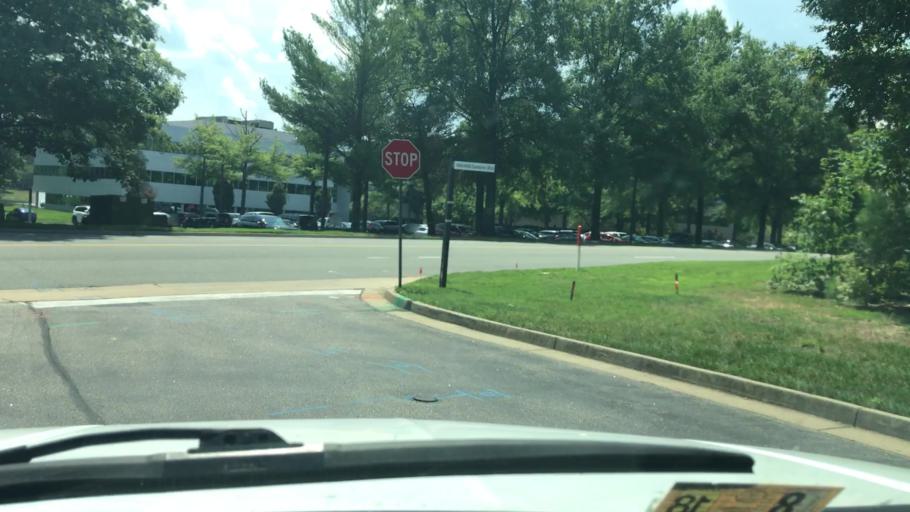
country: US
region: Virginia
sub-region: Henrico County
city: Short Pump
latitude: 37.6542
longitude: -77.5846
